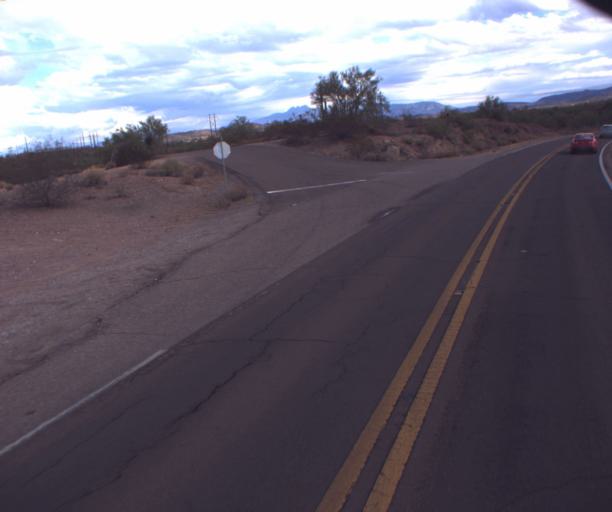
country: US
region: Arizona
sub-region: Pinal County
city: Apache Junction
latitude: 33.4447
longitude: -111.5102
